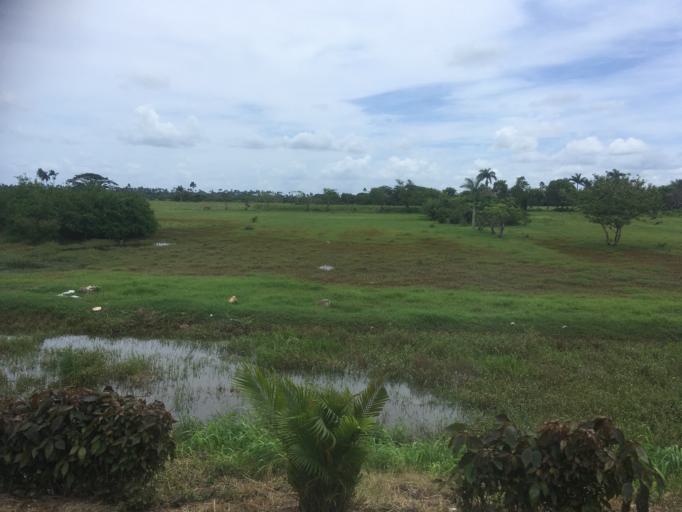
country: CU
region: Matanzas
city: Colon
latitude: 22.7113
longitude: -80.8933
